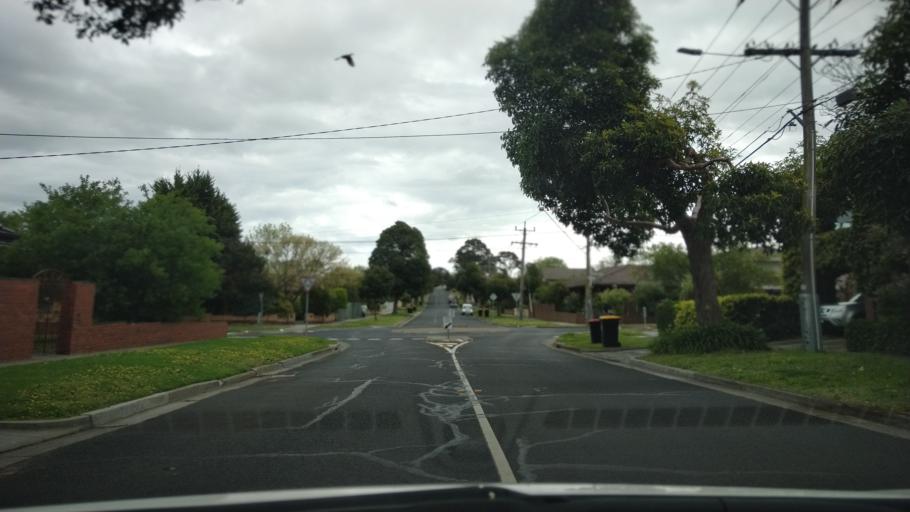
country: AU
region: Victoria
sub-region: Bayside
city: Cheltenham
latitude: -37.9644
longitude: 145.0657
